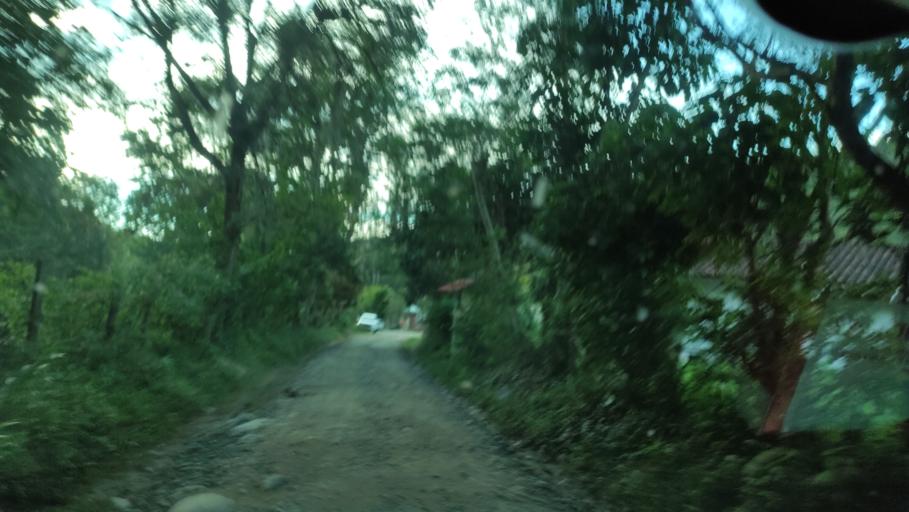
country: CO
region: Valle del Cauca
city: Buga
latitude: 3.8830
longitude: -76.1845
